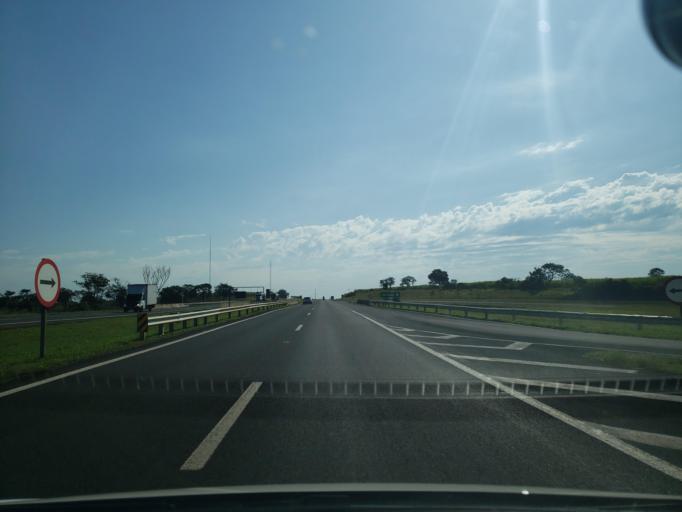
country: BR
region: Sao Paulo
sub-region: Penapolis
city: Penapolis
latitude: -21.5124
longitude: -50.0147
